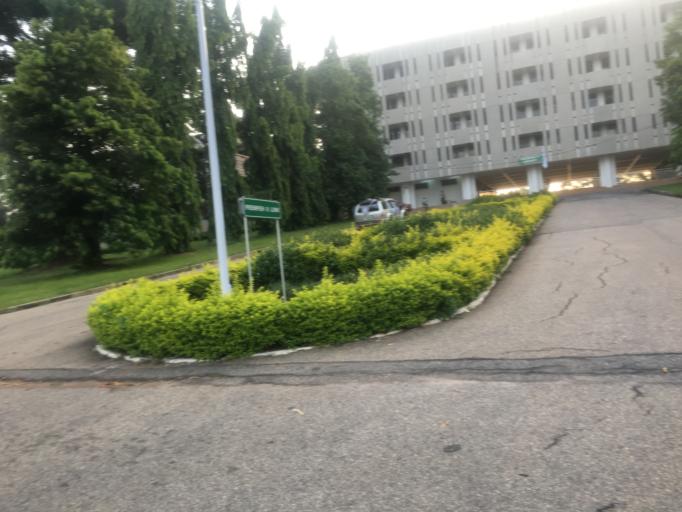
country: GH
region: Ashanti
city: Kumasi
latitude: 6.6752
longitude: -1.5724
